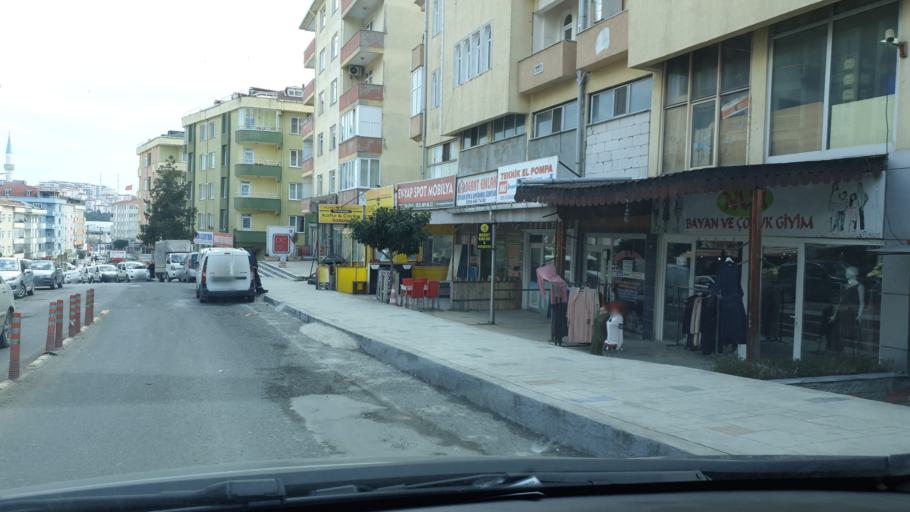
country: TR
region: Tekirdag
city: Cerkezkoey
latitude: 41.2839
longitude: 27.9945
